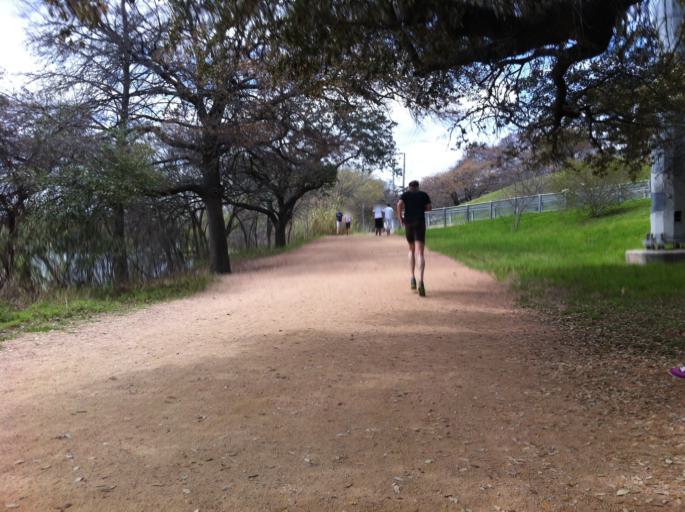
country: US
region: Texas
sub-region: Travis County
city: Austin
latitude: 30.2637
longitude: -97.7470
